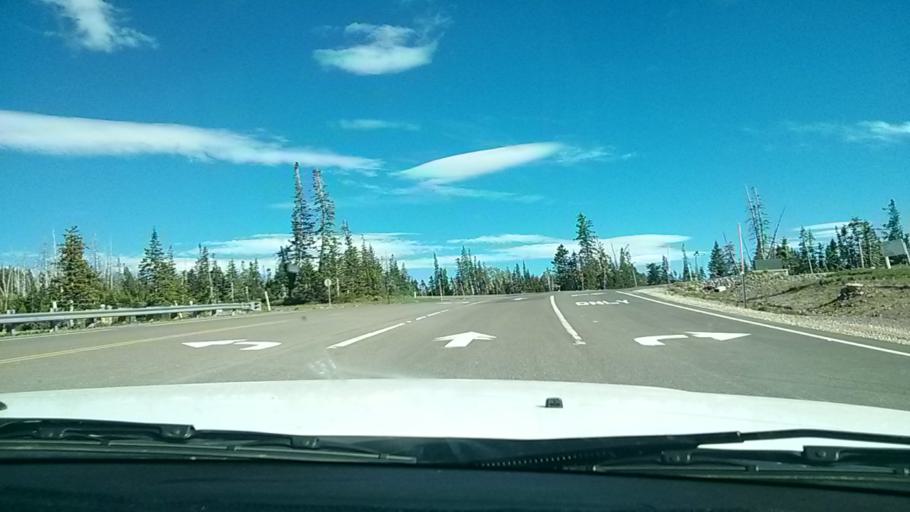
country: US
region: Utah
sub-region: Iron County
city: Parowan
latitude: 37.6793
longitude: -112.8486
